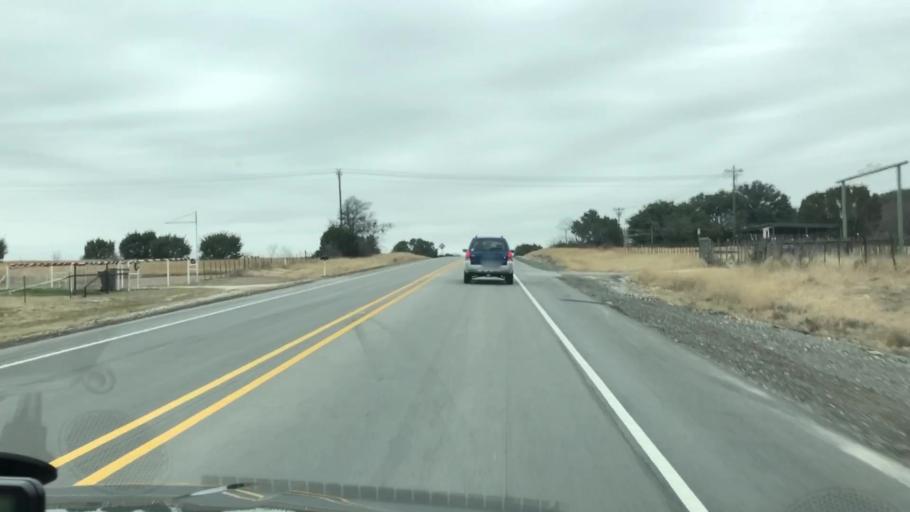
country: US
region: Texas
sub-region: Hamilton County
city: Hico
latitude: 32.0375
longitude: -98.0838
